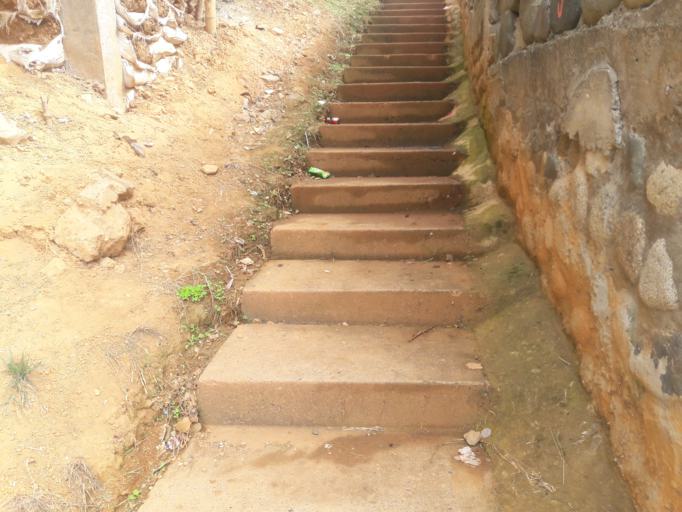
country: CO
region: Valle del Cauca
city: Cali
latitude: 3.4684
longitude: -76.6304
